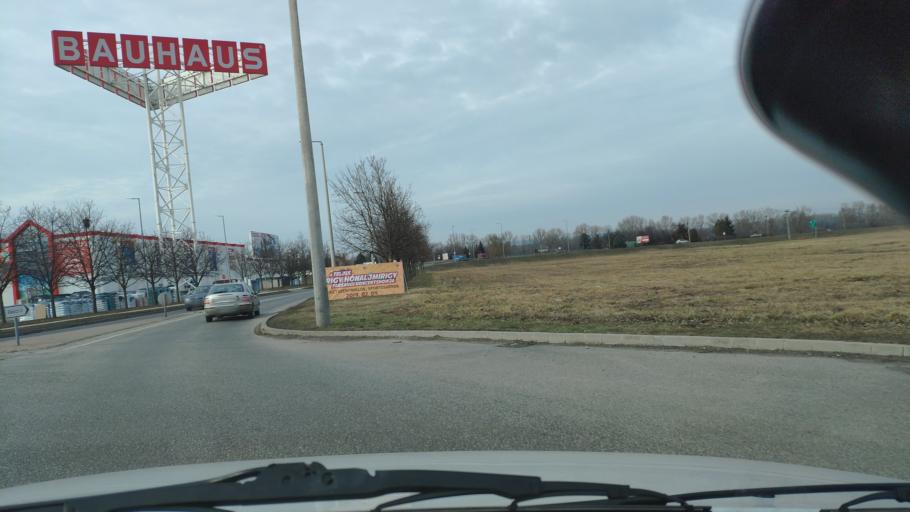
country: HU
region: Budapest
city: Budapest XXII. keruelet
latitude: 47.3850
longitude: 19.0257
